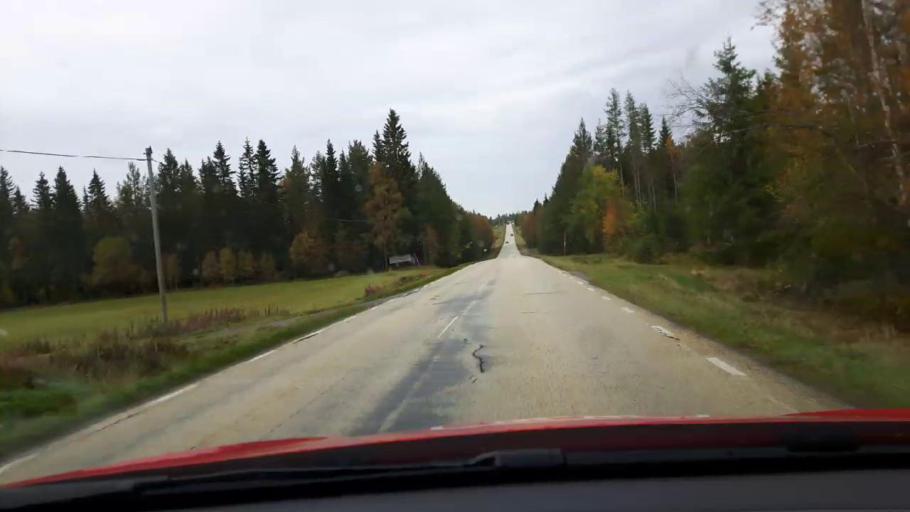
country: SE
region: Jaemtland
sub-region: Bergs Kommun
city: Hoverberg
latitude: 62.9289
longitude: 14.3352
